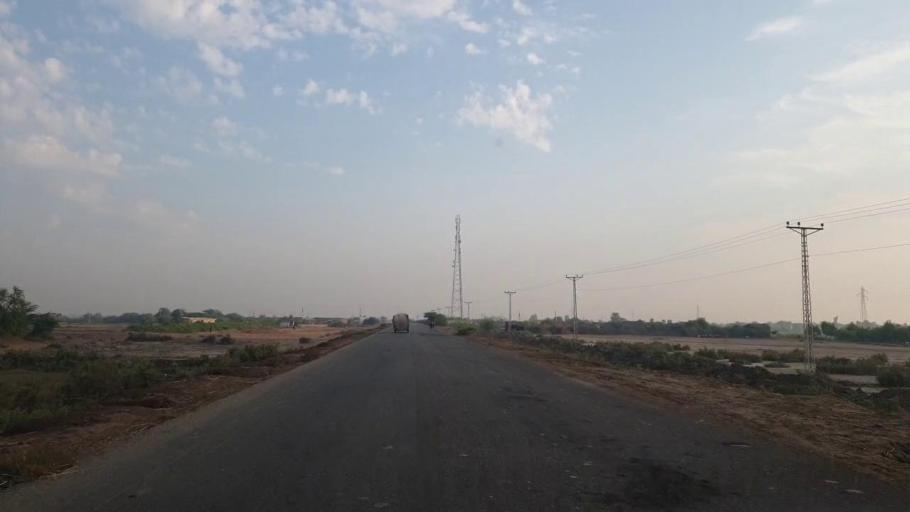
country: PK
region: Sindh
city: Badin
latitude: 24.6962
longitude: 68.9201
